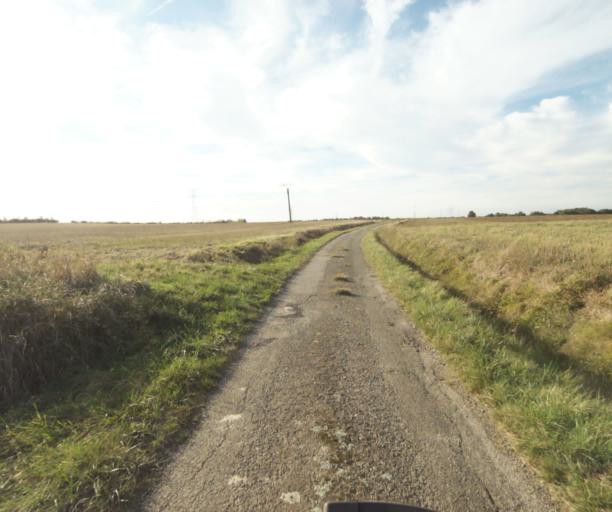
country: FR
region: Midi-Pyrenees
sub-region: Departement du Tarn-et-Garonne
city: Finhan
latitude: 43.9064
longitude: 1.1142
